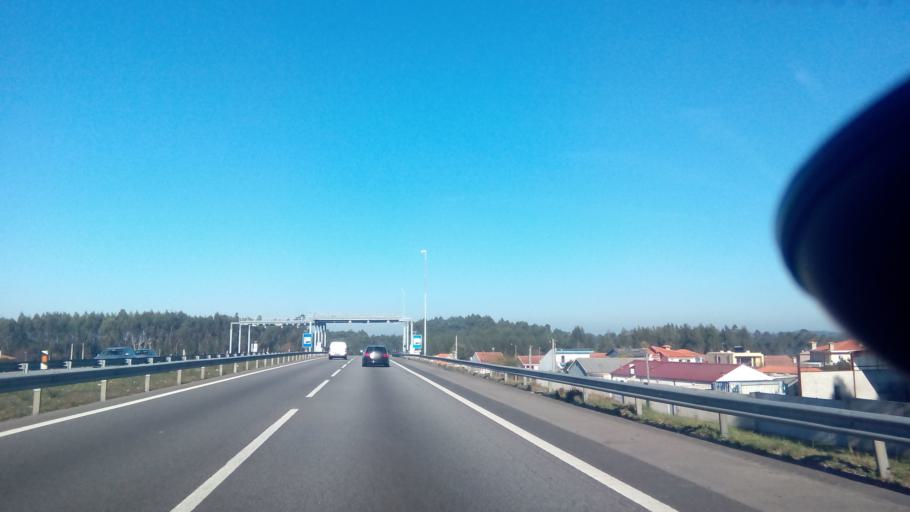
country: PT
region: Porto
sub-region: Matosinhos
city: Lavra
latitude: 41.2648
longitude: -8.7015
